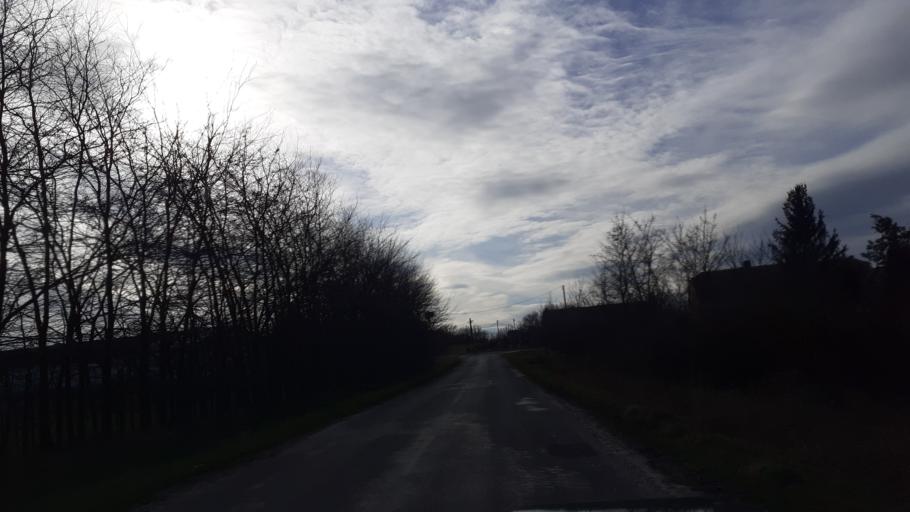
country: HU
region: Fejer
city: Kaloz
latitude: 46.9054
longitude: 18.5208
